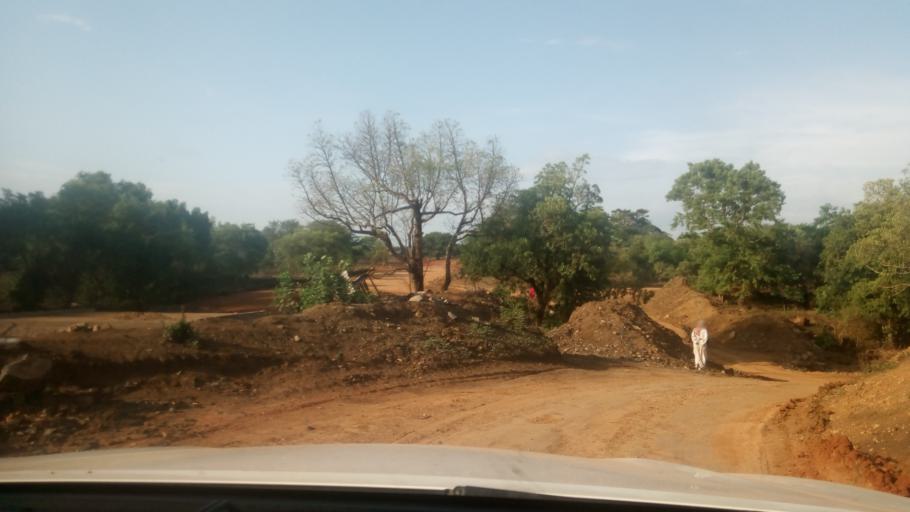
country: ET
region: Oromiya
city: Mendi
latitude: 10.2109
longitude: 35.0812
